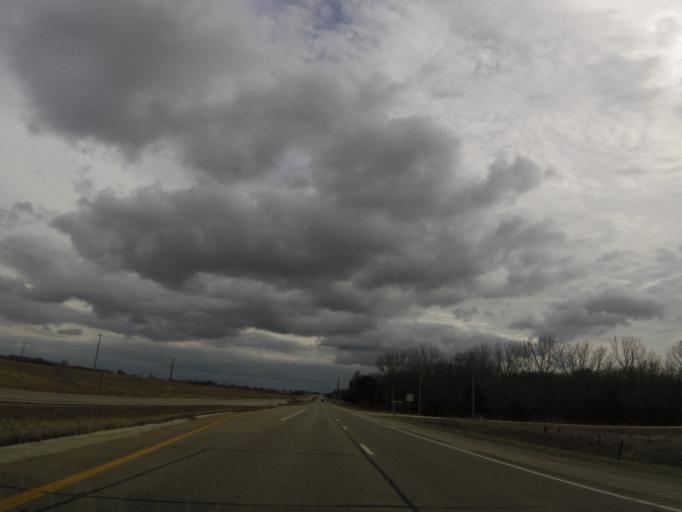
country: US
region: Iowa
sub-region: Bremer County
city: Denver
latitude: 42.6006
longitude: -92.3374
